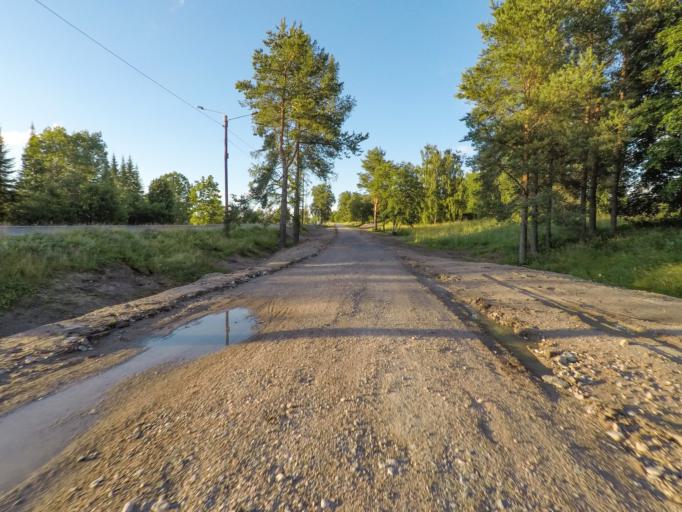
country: FI
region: South Karelia
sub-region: Imatra
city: Imatra
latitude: 61.2017
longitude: 28.7867
